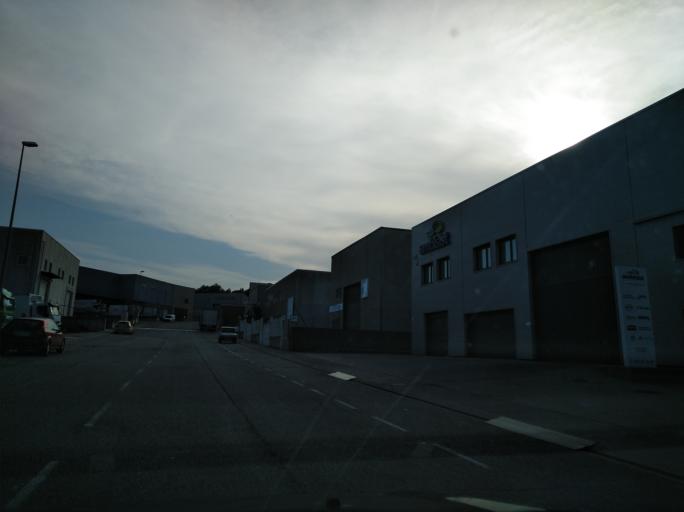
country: ES
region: Catalonia
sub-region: Provincia de Girona
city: Vilablareix
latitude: 41.9420
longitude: 2.7791
